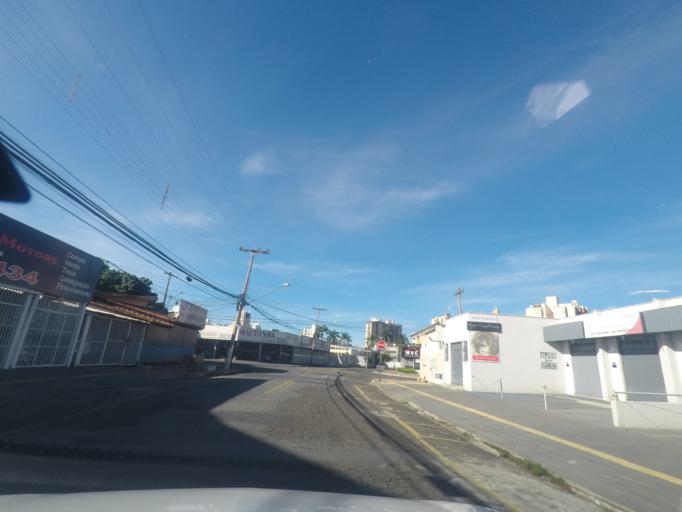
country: BR
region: Goias
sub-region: Goiania
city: Goiania
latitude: -16.6719
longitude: -49.2682
